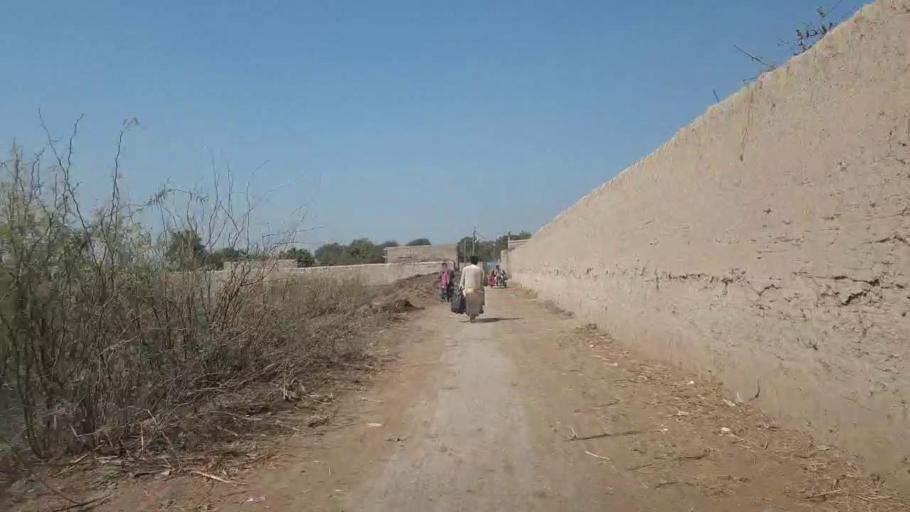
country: PK
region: Sindh
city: Tando Jam
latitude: 25.3289
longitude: 68.6290
